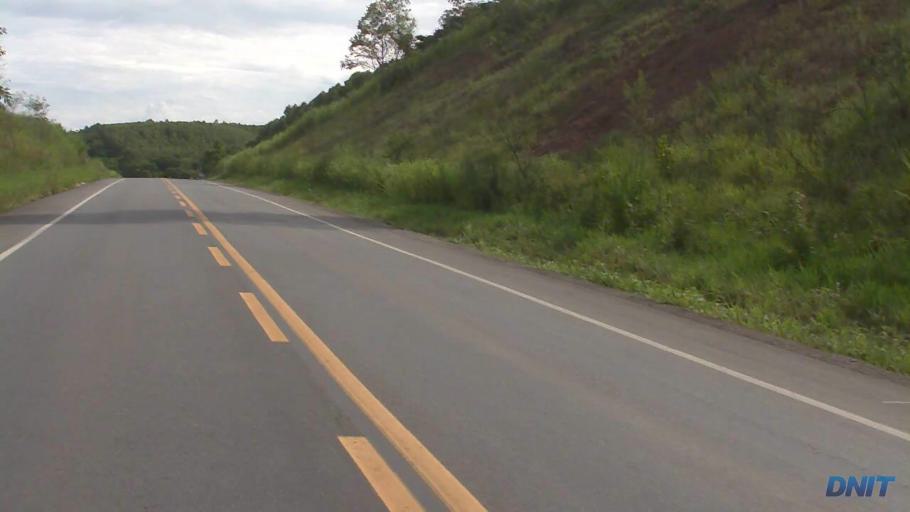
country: BR
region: Minas Gerais
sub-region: Belo Oriente
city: Belo Oriente
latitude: -19.2466
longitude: -42.3378
